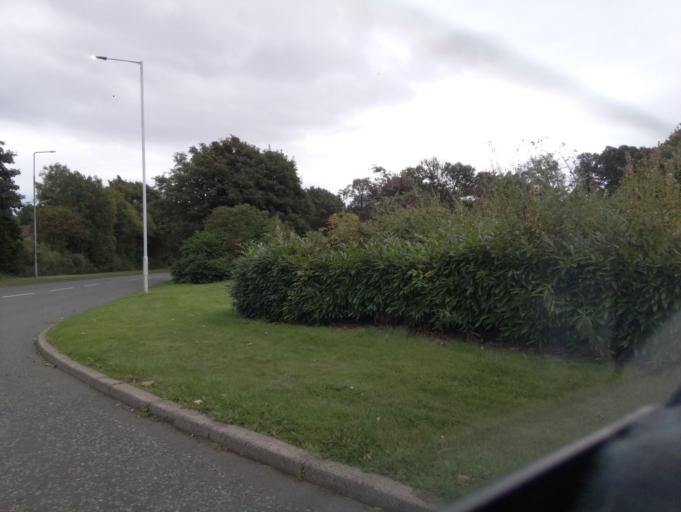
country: GB
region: Scotland
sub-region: Fife
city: Glenrothes
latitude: 56.2044
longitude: -3.1878
